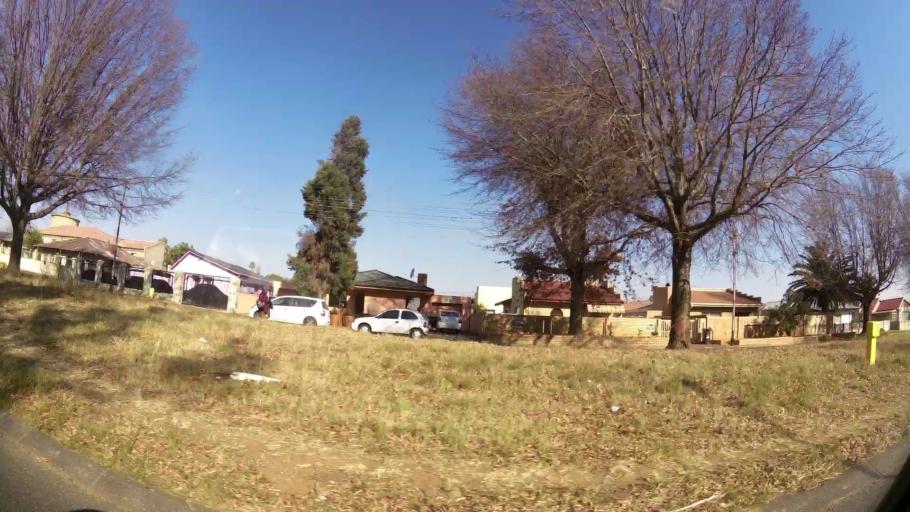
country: ZA
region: Gauteng
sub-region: City of Johannesburg Metropolitan Municipality
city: Johannesburg
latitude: -26.2566
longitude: 28.0053
